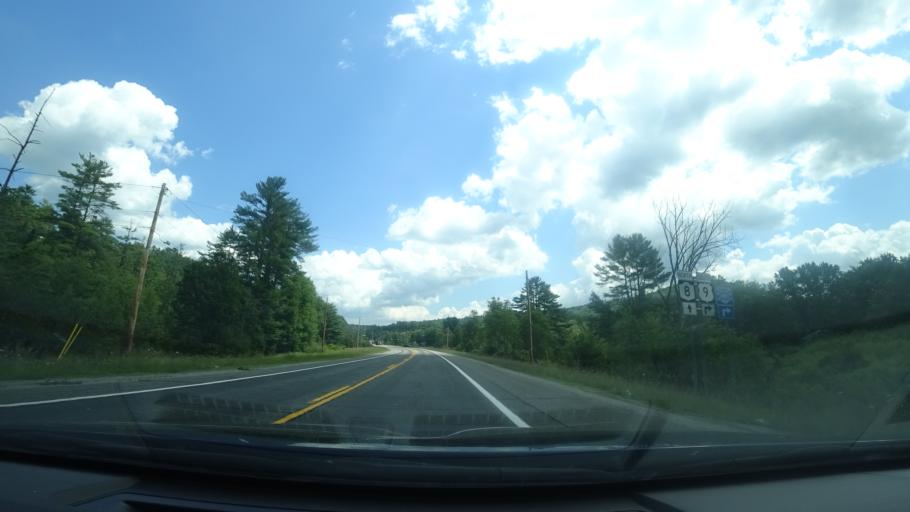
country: US
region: New York
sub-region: Warren County
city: Warrensburg
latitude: 43.6558
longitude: -73.8048
